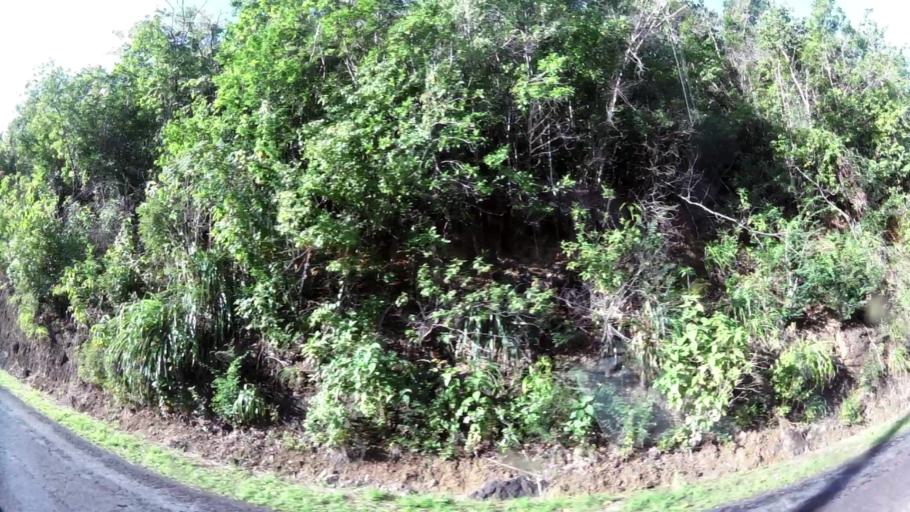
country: LC
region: Anse-la-Raye
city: Anse La Raye
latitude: 13.9268
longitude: -61.0441
